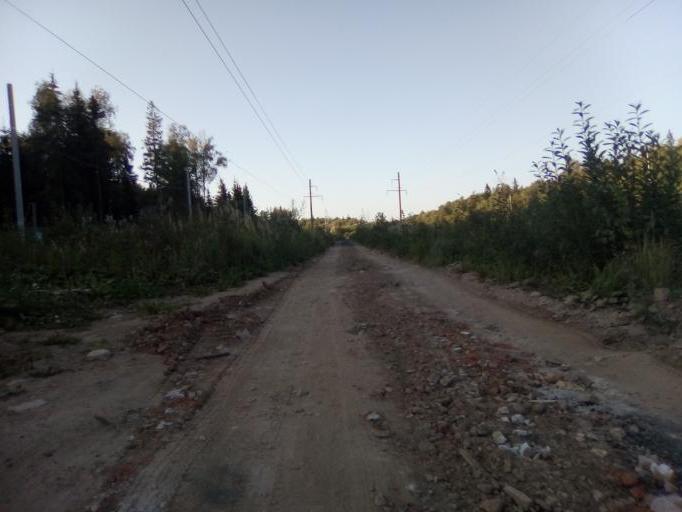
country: RU
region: Moskovskaya
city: Aprelevka
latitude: 55.5760
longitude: 37.0656
